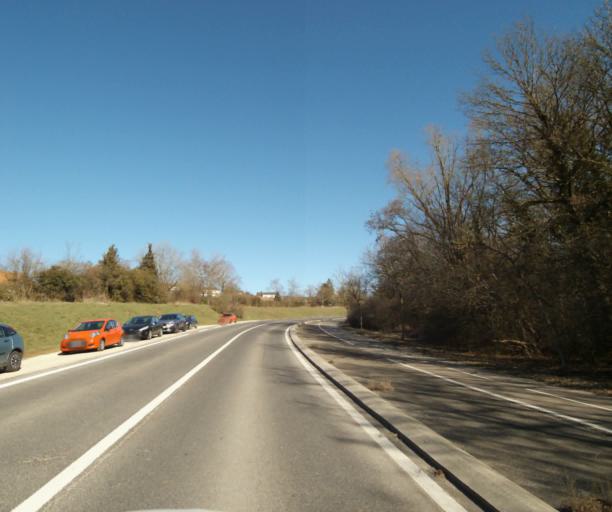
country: FR
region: Lorraine
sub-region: Departement de Meurthe-et-Moselle
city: Richardmenil
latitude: 48.6113
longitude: 6.1744
